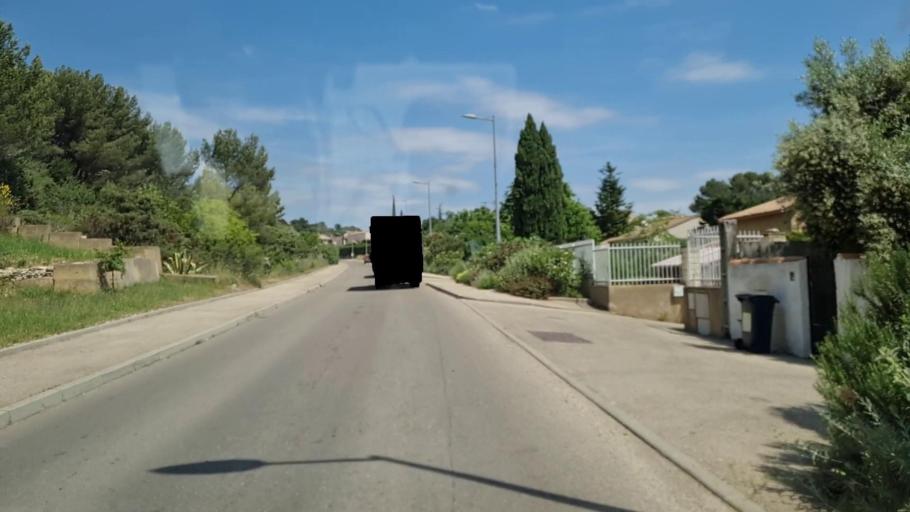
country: FR
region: Languedoc-Roussillon
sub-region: Departement du Gard
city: Cabrieres
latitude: 43.9007
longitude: 4.4737
